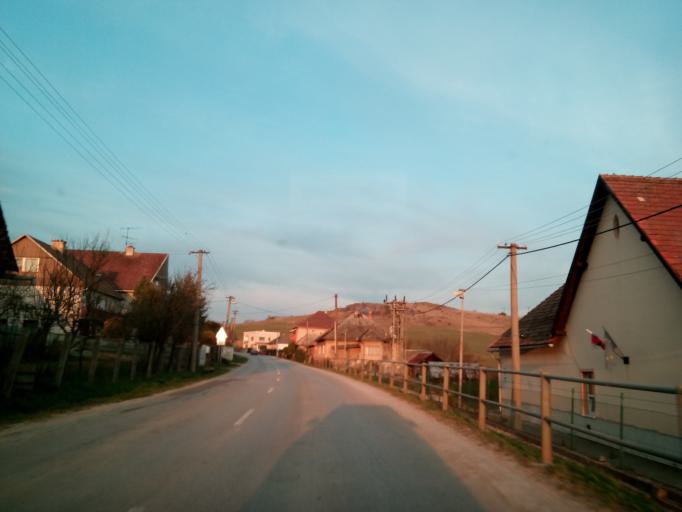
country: SK
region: Kosicky
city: Roznava
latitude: 48.6594
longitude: 20.4913
